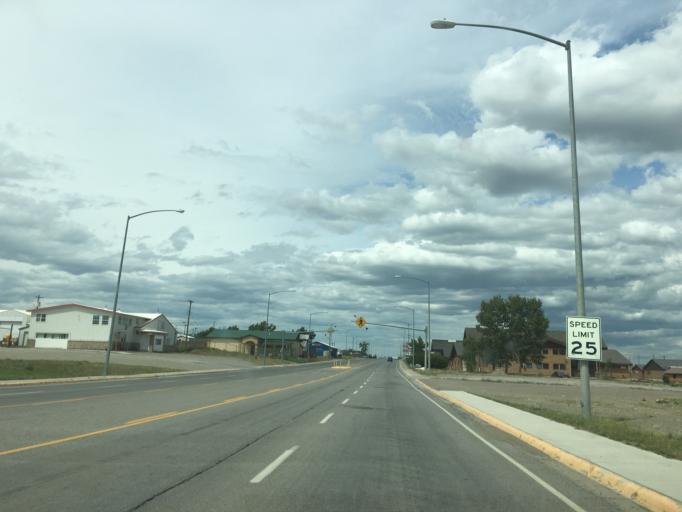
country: US
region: Montana
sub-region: Glacier County
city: South Browning
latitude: 48.5504
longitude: -113.0098
